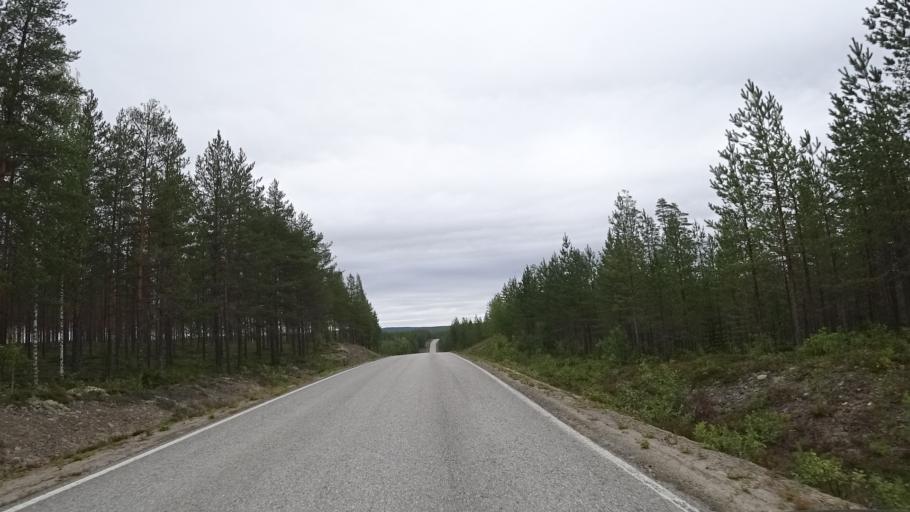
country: FI
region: North Karelia
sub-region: Pielisen Karjala
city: Lieksa
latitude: 63.3782
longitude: 30.3127
